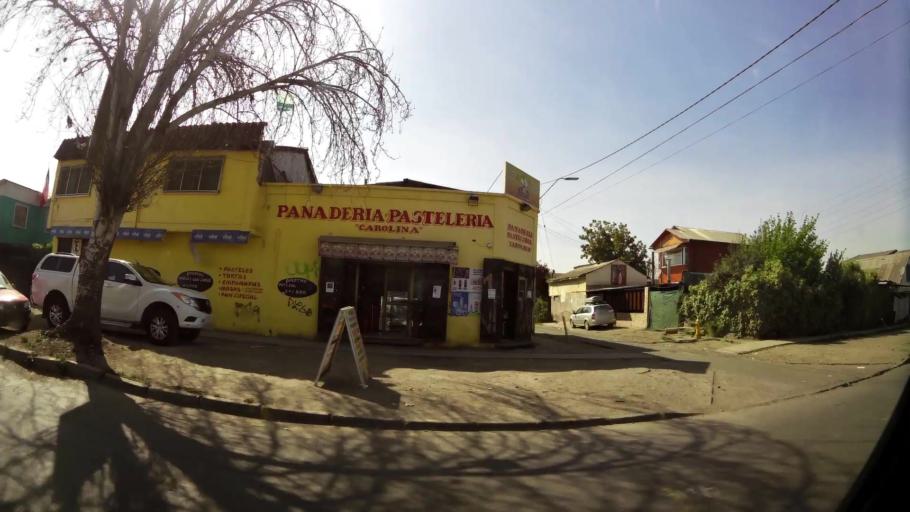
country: CL
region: Santiago Metropolitan
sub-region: Provincia de Santiago
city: Lo Prado
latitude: -33.4211
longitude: -70.7475
